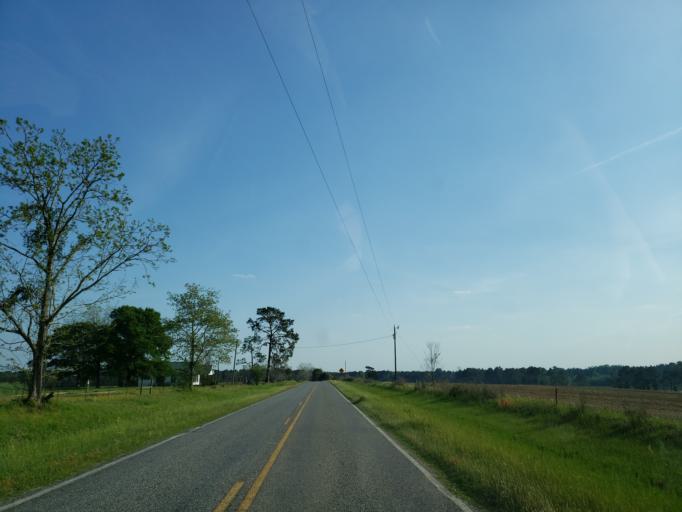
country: US
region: Georgia
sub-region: Tift County
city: Tifton
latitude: 31.5046
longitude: -83.5602
